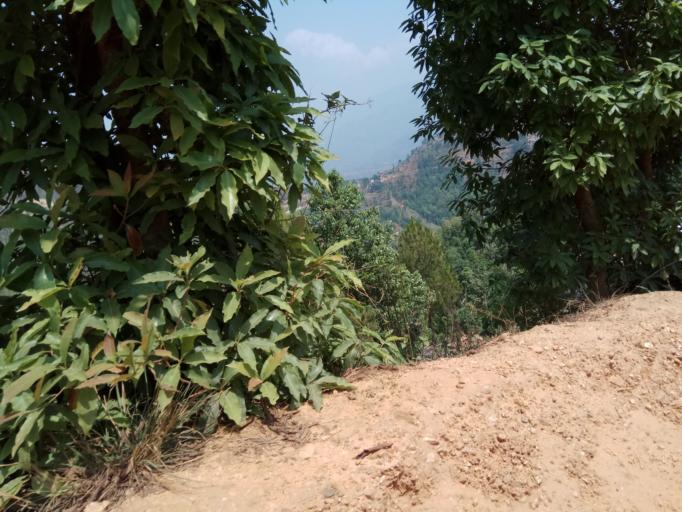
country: NP
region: Central Region
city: Kirtipur
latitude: 27.8914
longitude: 85.0822
